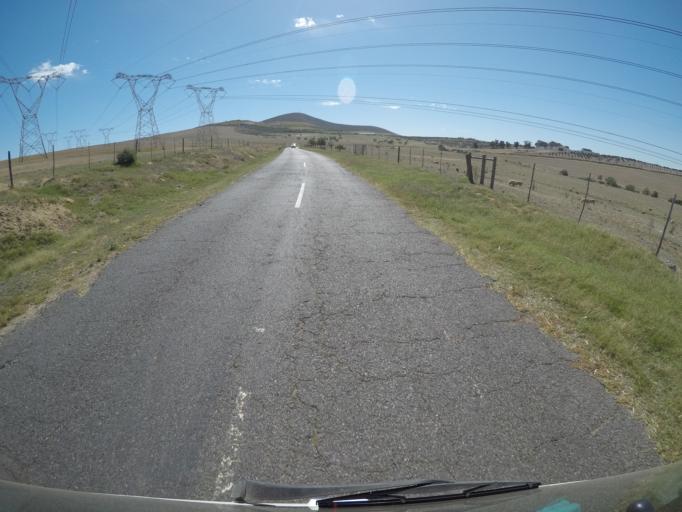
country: ZA
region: Western Cape
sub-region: City of Cape Town
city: Sunset Beach
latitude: -33.7321
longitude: 18.5657
